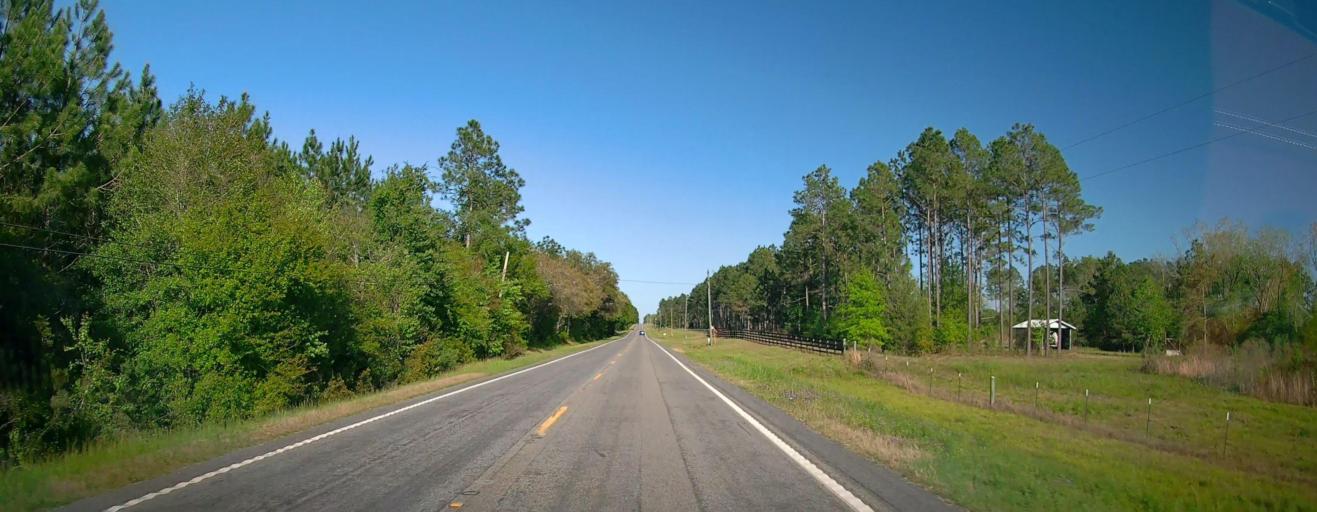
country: US
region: Georgia
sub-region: Ben Hill County
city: Fitzgerald
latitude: 31.7191
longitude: -83.3643
